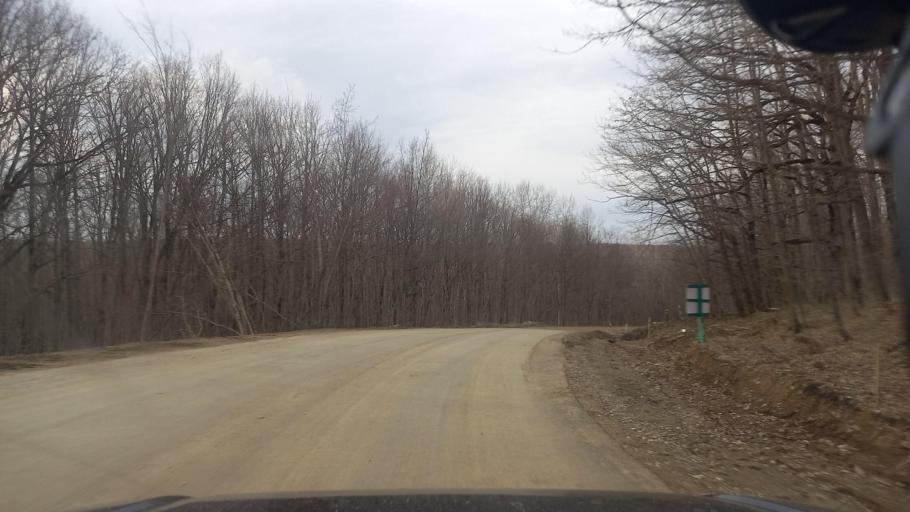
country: RU
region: Krasnodarskiy
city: Goryachiy Klyuch
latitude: 44.7007
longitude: 39.0175
